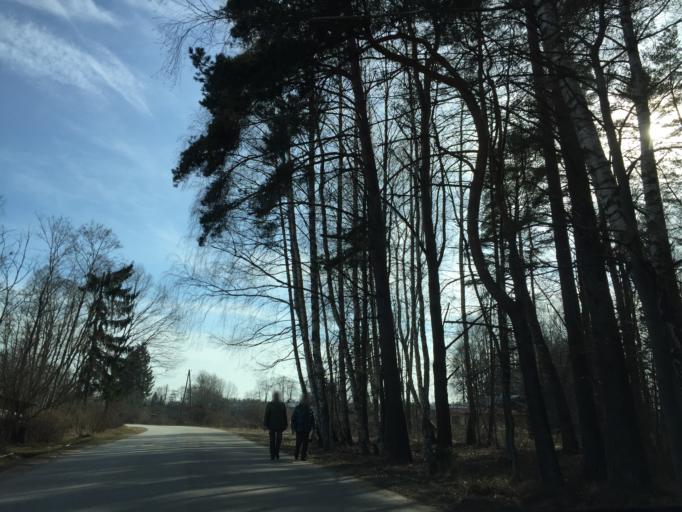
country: LV
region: Saulkrastu
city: Saulkrasti
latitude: 57.2761
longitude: 24.4558
